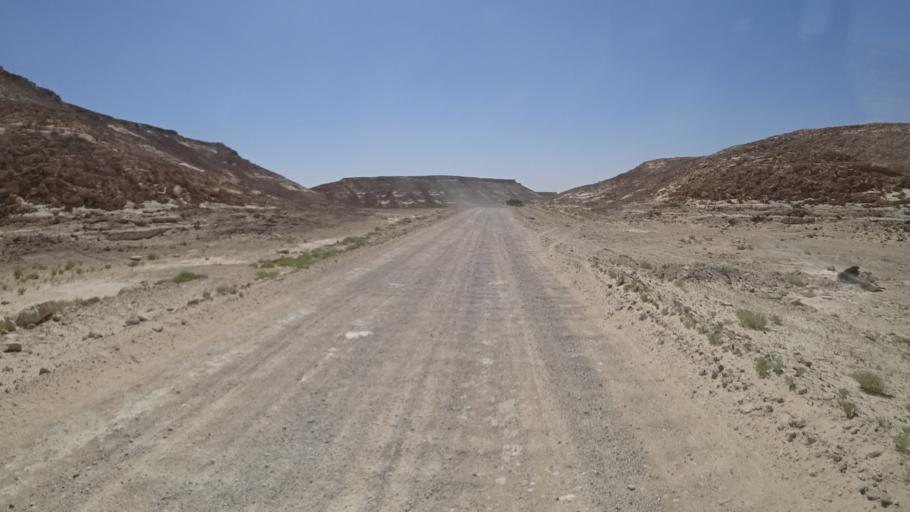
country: OM
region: Zufar
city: Salalah
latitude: 17.4677
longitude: 53.3429
